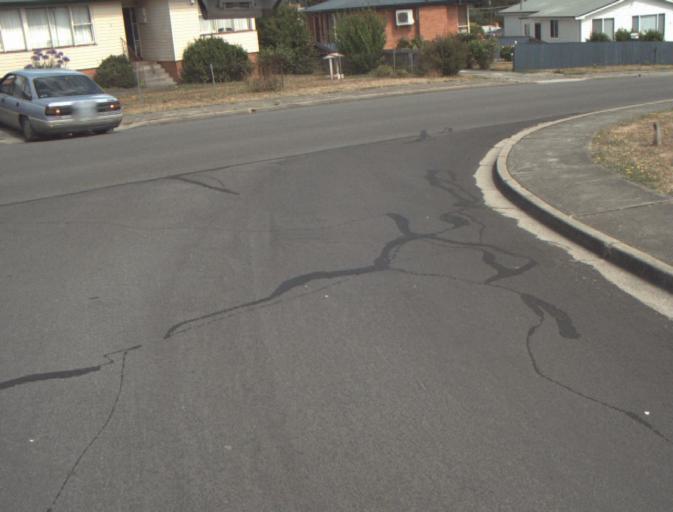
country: AU
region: Tasmania
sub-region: Launceston
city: Newstead
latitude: -41.4199
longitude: 147.1752
